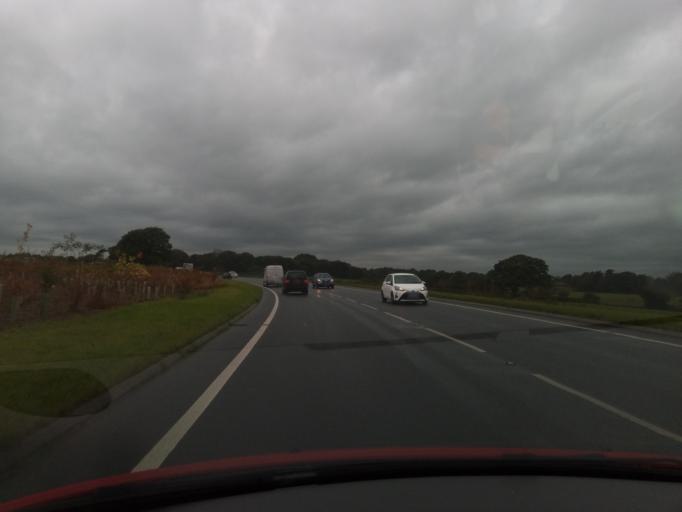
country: GB
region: England
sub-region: Lancashire
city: Preston
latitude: 53.8135
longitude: -2.7215
